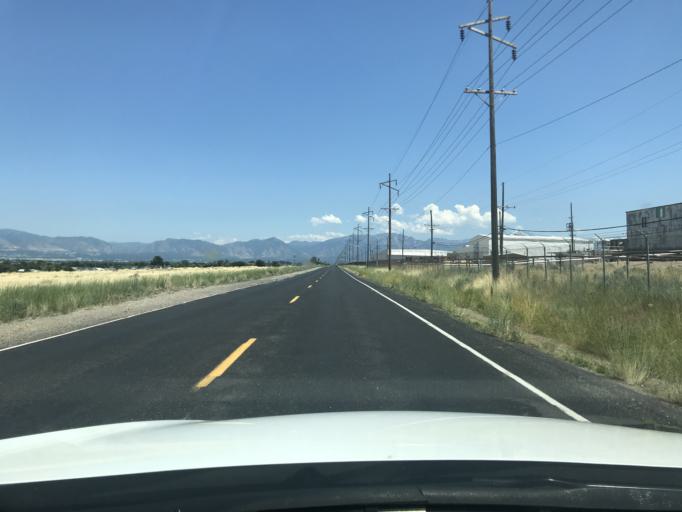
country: US
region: Utah
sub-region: Salt Lake County
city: Magna
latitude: 40.6820
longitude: -112.0701
